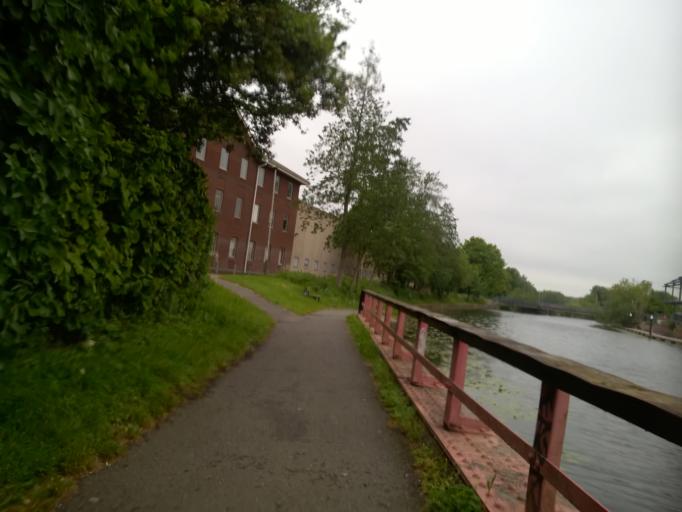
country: GB
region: England
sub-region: City of Leicester
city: Leicester
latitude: 52.6360
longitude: -1.1448
